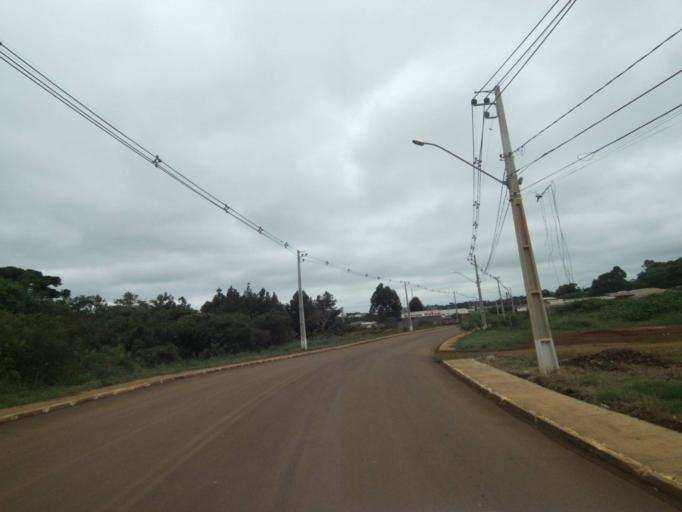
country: BR
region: Parana
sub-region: Pitanga
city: Pitanga
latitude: -24.9291
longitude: -51.8738
